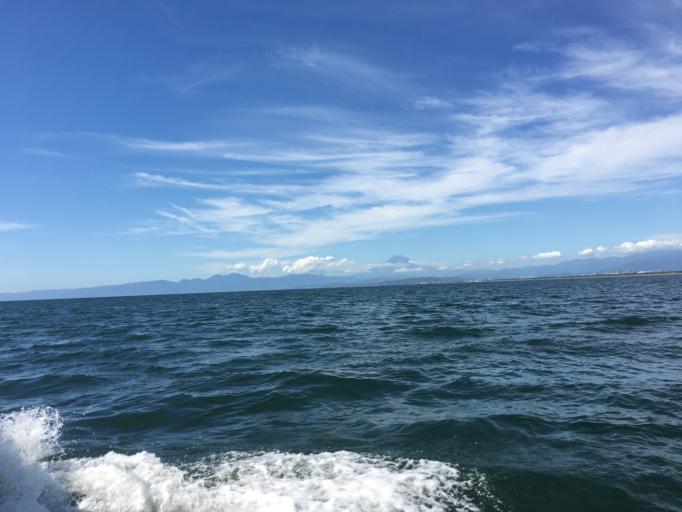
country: JP
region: Kanagawa
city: Fujisawa
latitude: 35.3033
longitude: 139.4779
